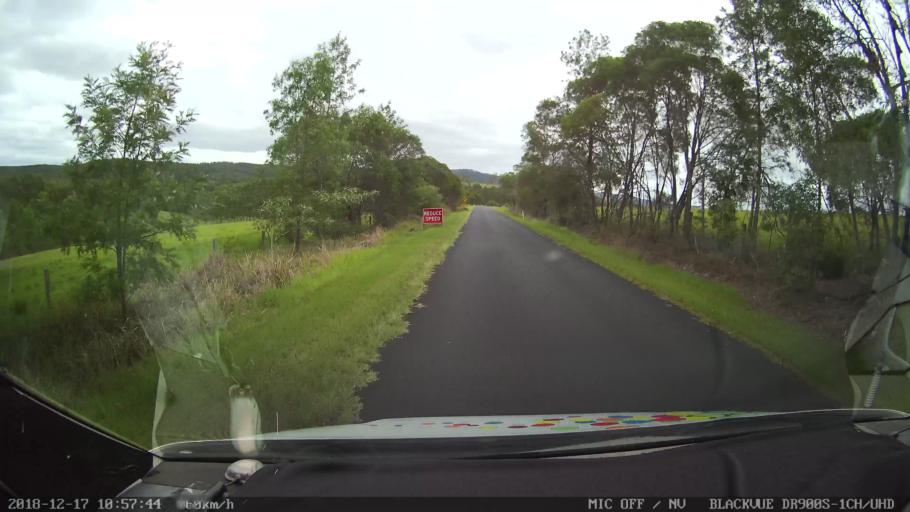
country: AU
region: New South Wales
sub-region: Richmond Valley
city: Casino
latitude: -28.8234
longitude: 152.5991
